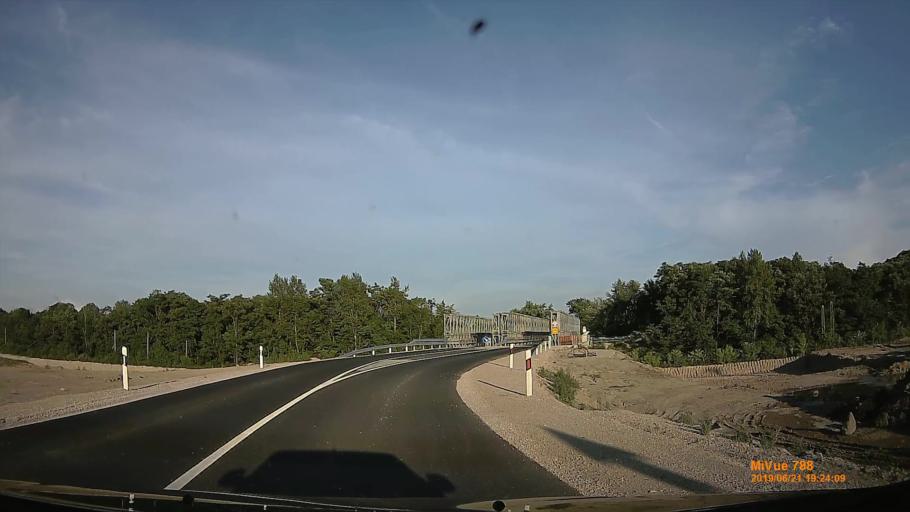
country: HU
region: Pest
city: Szazhalombatta
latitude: 47.3009
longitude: 18.8883
